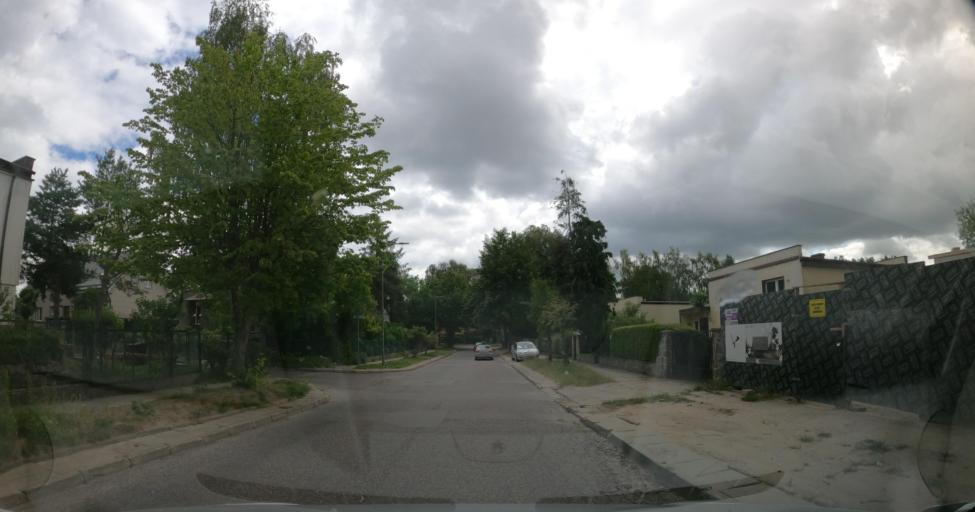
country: PL
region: Pomeranian Voivodeship
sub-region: Gdynia
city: Wielki Kack
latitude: 54.4263
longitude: 18.4684
